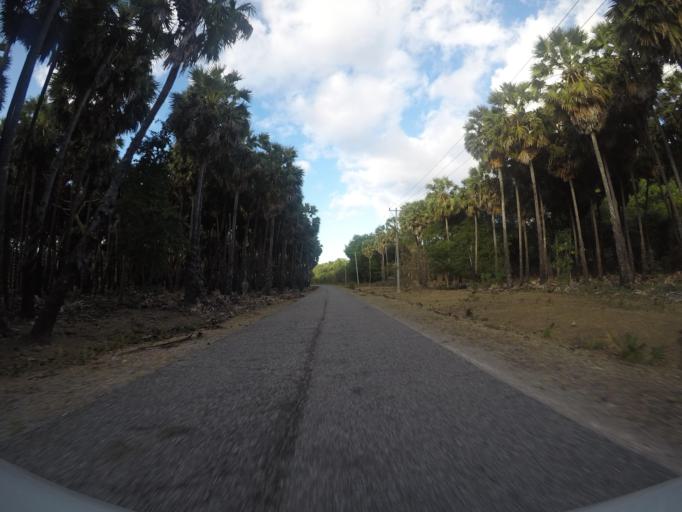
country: TL
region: Lautem
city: Lospalos
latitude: -8.3332
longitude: 126.9555
